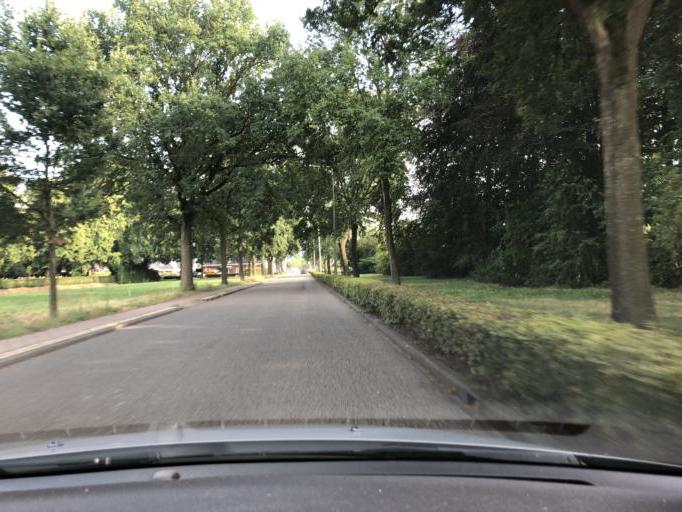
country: NL
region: Overijssel
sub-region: Gemeente Dalfsen
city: Dalfsen
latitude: 52.5789
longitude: 6.2892
